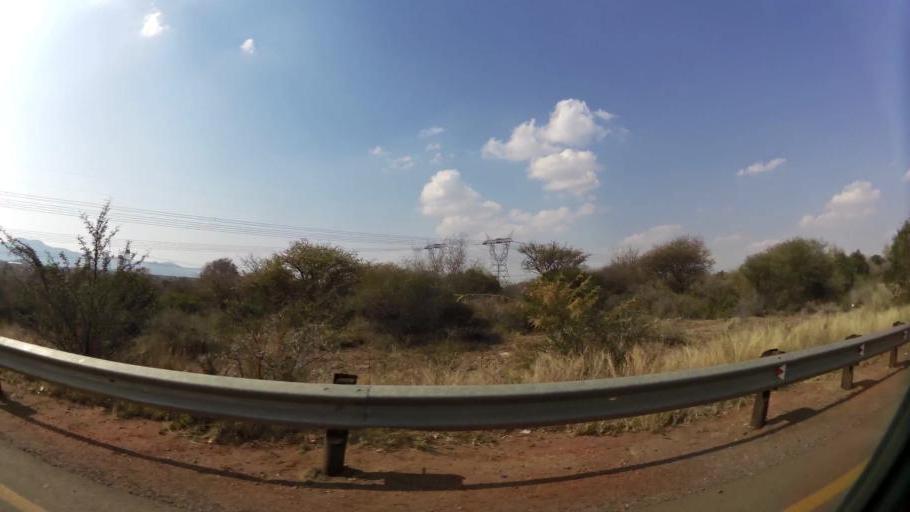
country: ZA
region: North-West
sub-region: Bojanala Platinum District Municipality
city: Mogwase
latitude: -25.3951
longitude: 27.0716
